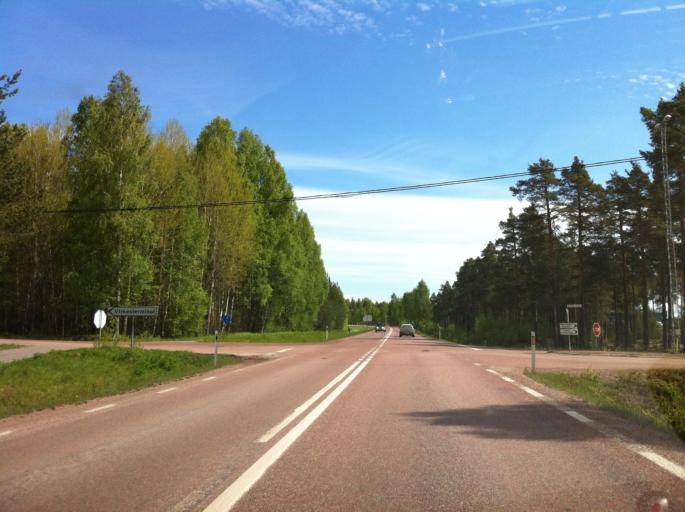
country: SE
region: Dalarna
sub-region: Mora Kommun
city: Mora
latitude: 60.9792
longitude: 14.5138
